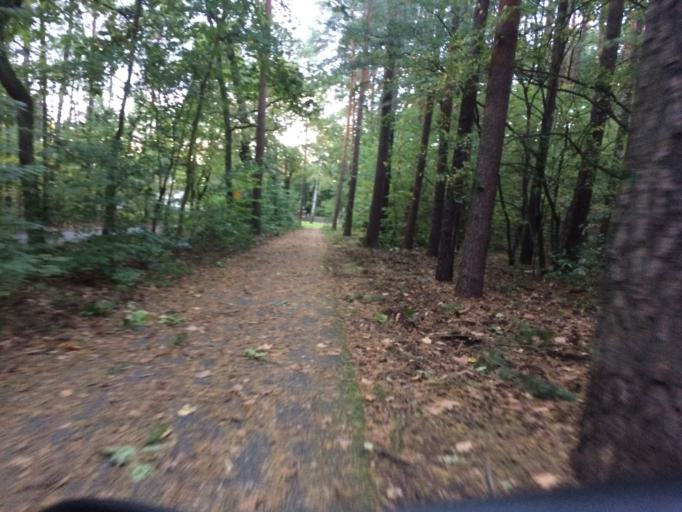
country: DE
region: Brandenburg
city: Birkenwerder
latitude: 52.7134
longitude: 13.2830
